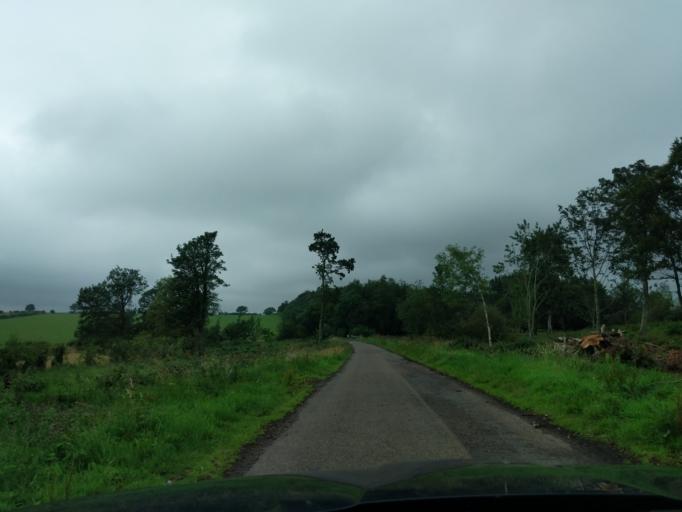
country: GB
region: England
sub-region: Northumberland
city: Ford
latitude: 55.6781
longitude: -2.1197
